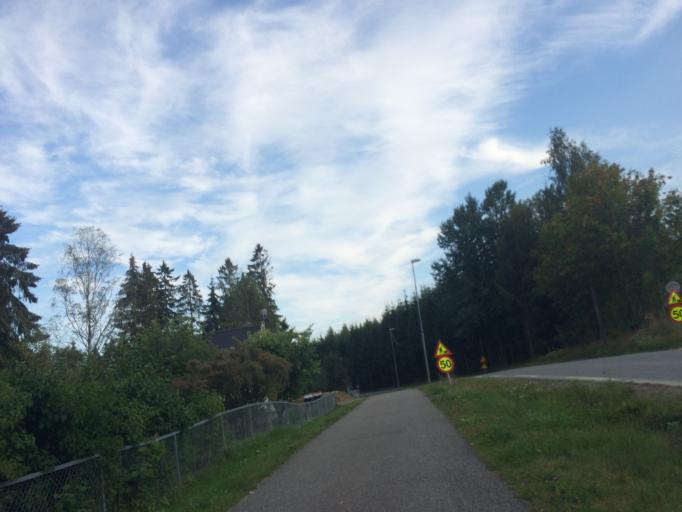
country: NO
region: Akershus
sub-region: Ski
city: Ski
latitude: 59.6998
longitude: 10.8462
